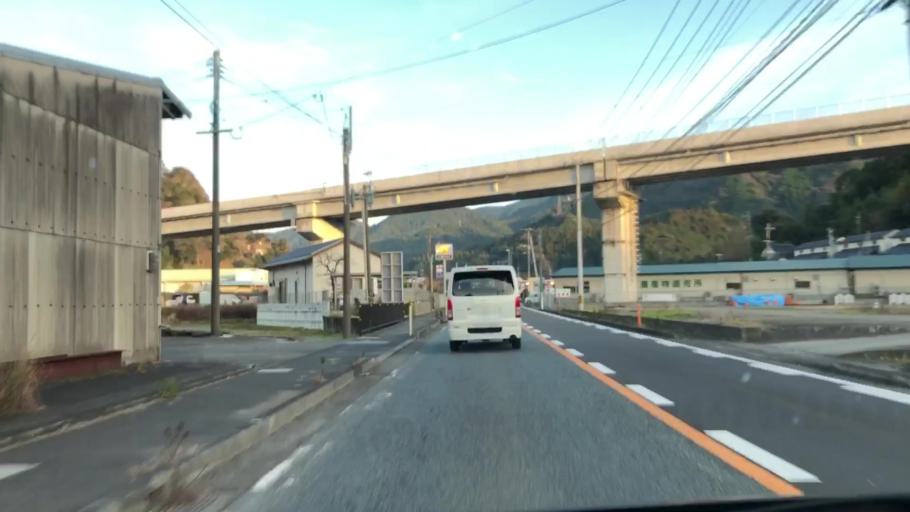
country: JP
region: Kumamoto
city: Minamata
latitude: 32.2329
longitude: 130.4519
